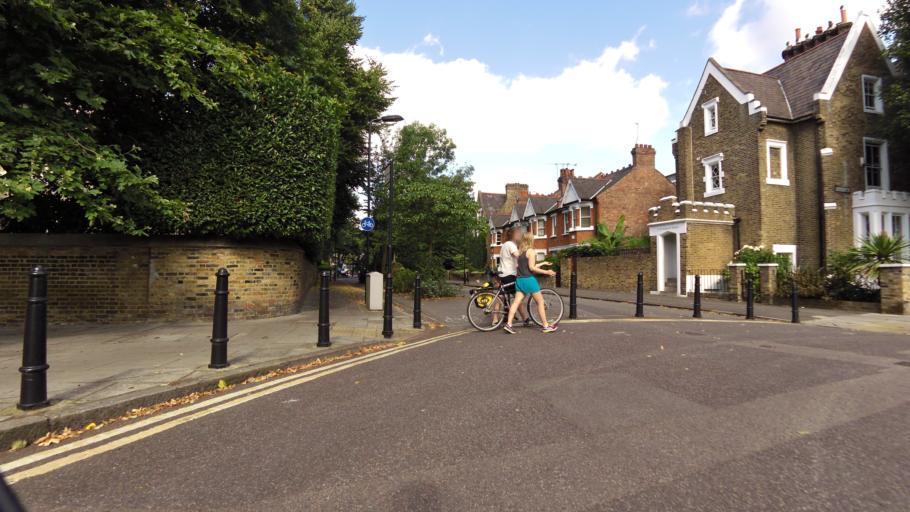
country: GB
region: England
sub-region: Greater London
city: Bethnal Green
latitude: 51.5409
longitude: -0.0795
